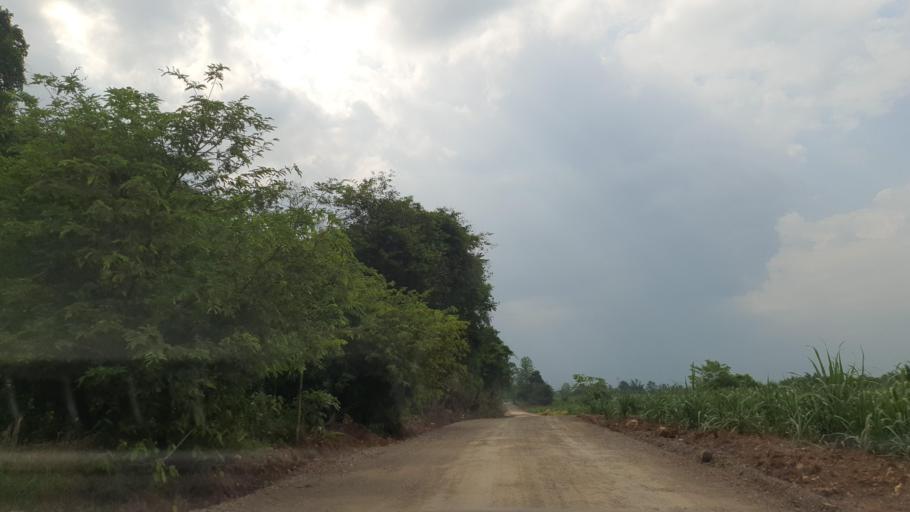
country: TH
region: Sukhothai
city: Thung Saliam
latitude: 17.2559
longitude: 99.5414
